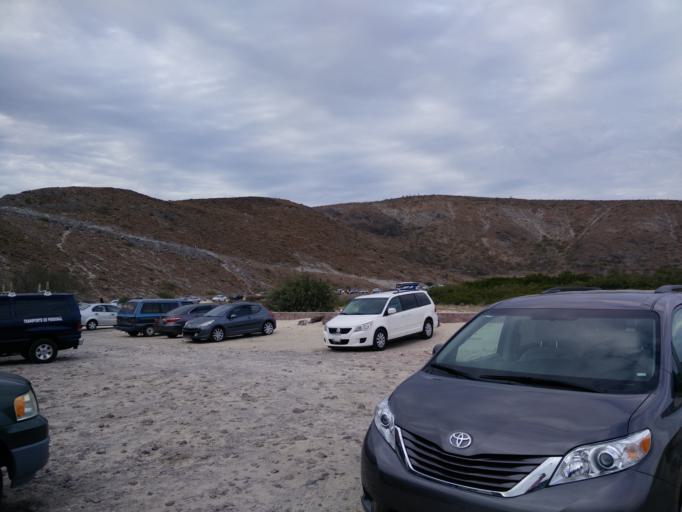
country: MX
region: Baja California Sur
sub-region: La Paz
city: La Paz
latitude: 24.3222
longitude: -110.3245
